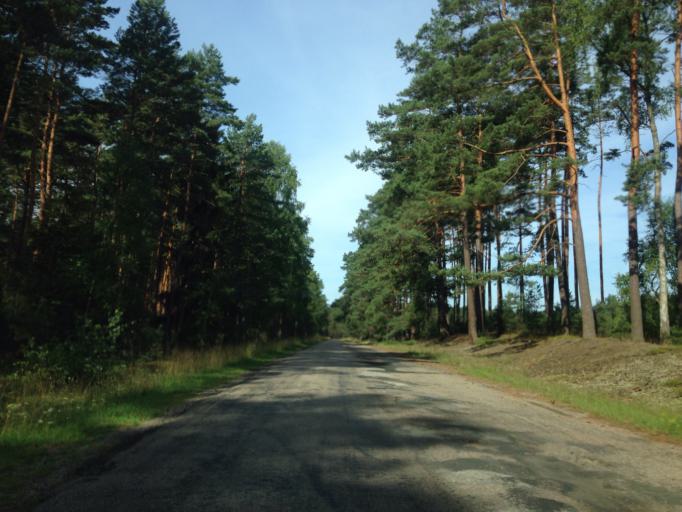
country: PL
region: Kujawsko-Pomorskie
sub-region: Powiat swiecki
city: Osie
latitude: 53.7005
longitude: 18.3379
